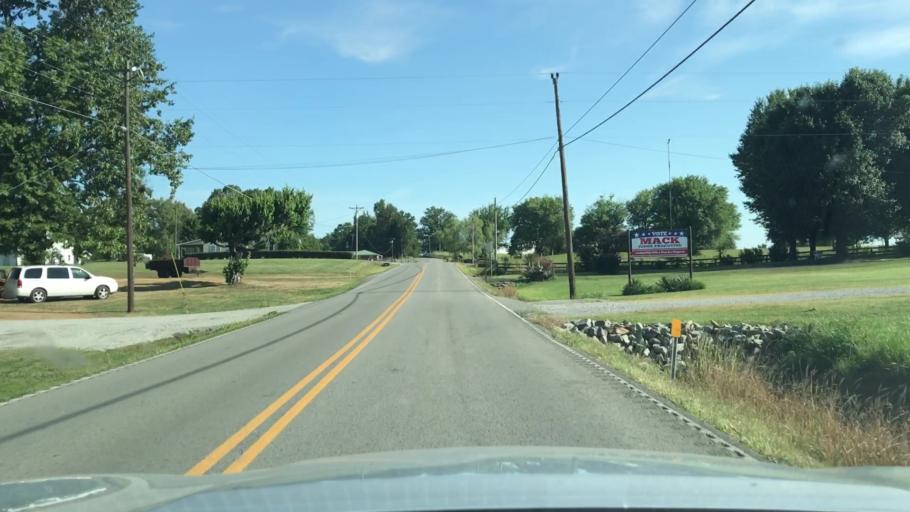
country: US
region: Kentucky
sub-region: Muhlenberg County
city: Greenville
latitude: 37.1571
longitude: -87.1420
